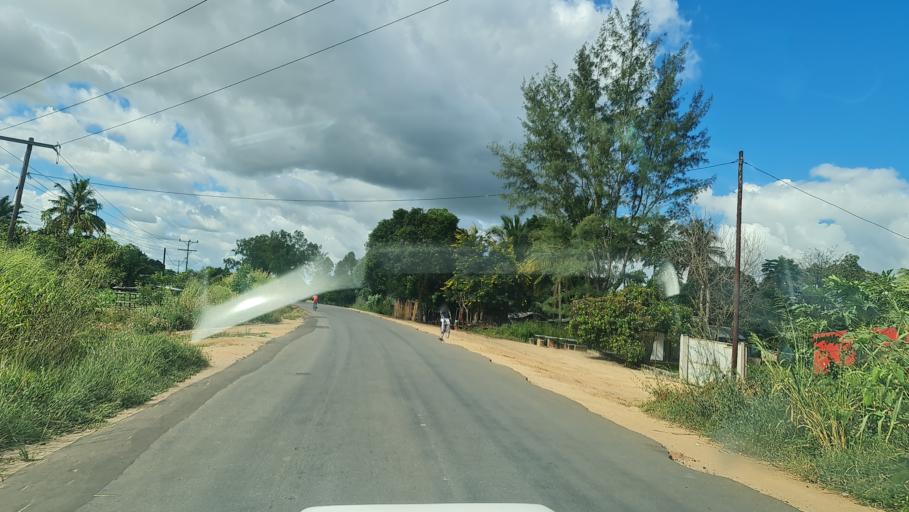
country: MZ
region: Zambezia
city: Quelimane
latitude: -17.6009
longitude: 36.8042
